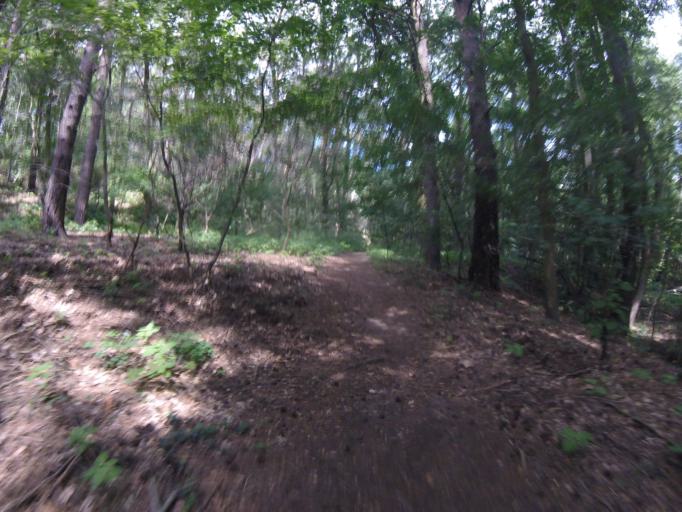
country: DE
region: Brandenburg
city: Bestensee
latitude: 52.2540
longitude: 13.6070
